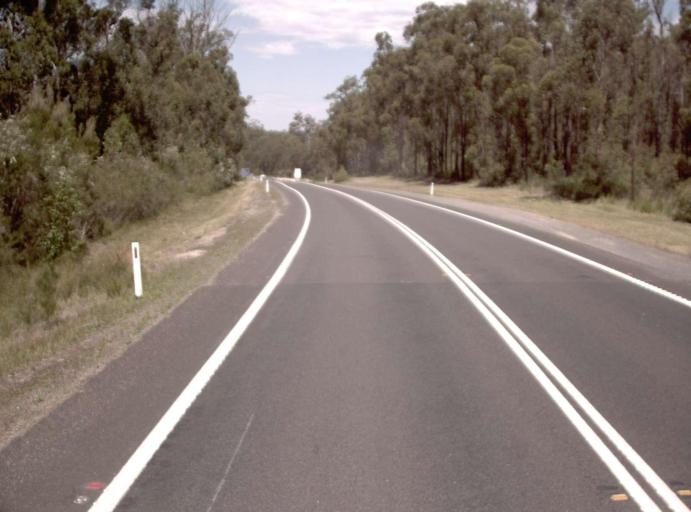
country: AU
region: New South Wales
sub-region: Bombala
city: Bombala
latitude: -37.5665
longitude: 149.1247
